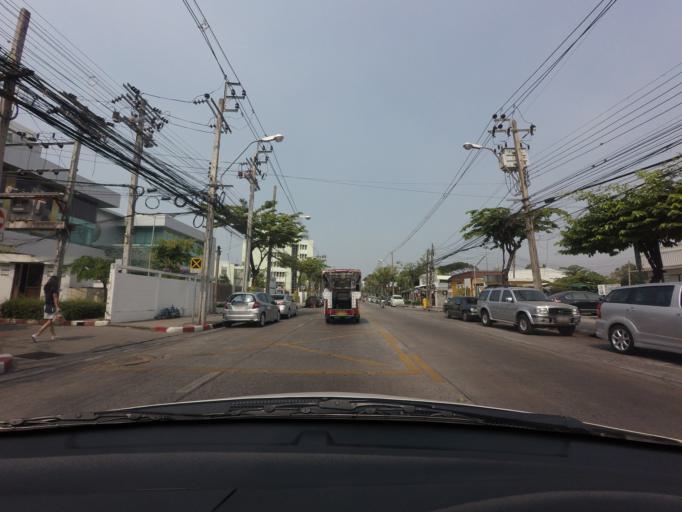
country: TH
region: Bangkok
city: Bangkok Noi
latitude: 13.7707
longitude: 100.4685
